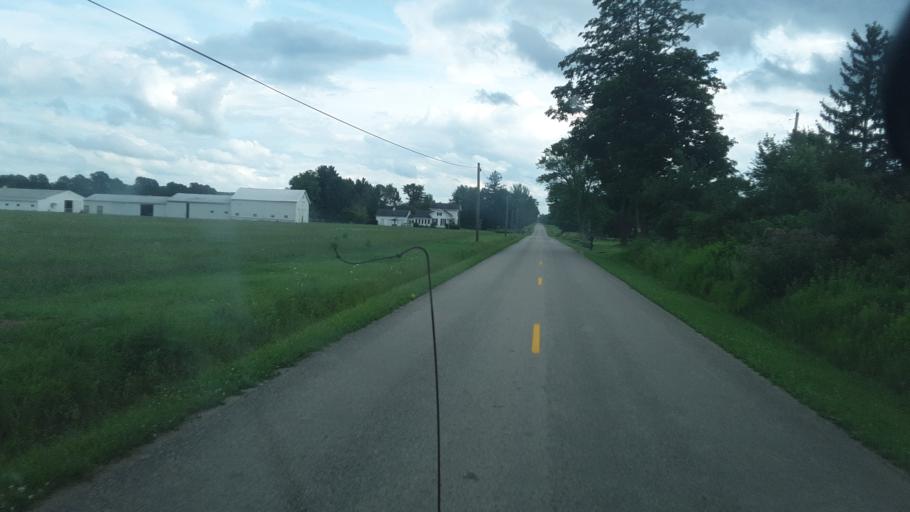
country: US
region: Ohio
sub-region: Ashtabula County
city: Jefferson
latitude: 41.6700
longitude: -80.7221
